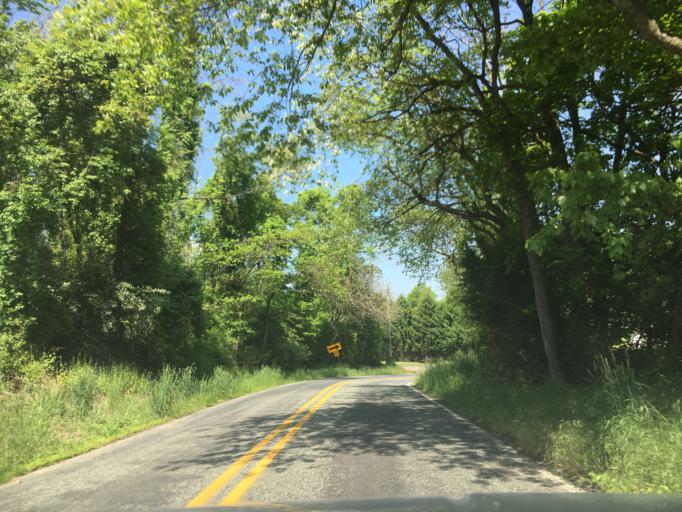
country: US
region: Pennsylvania
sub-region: Berks County
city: Fleetwood
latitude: 40.4446
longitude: -75.7783
